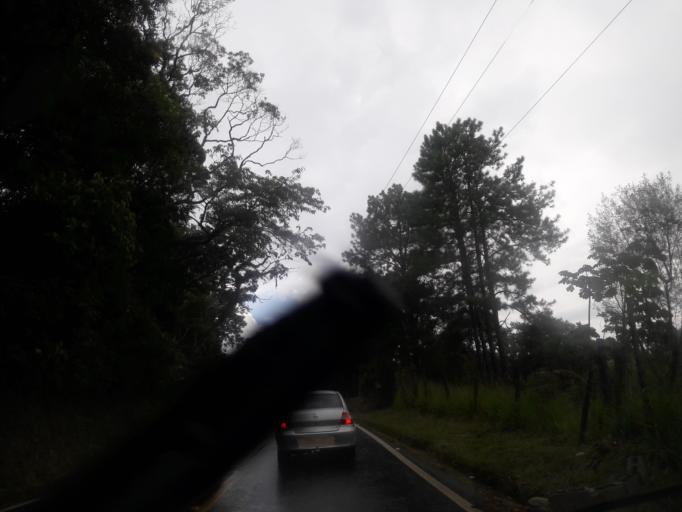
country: BR
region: Sao Paulo
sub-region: Aruja
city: Aruja
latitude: -23.3197
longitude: -46.4366
